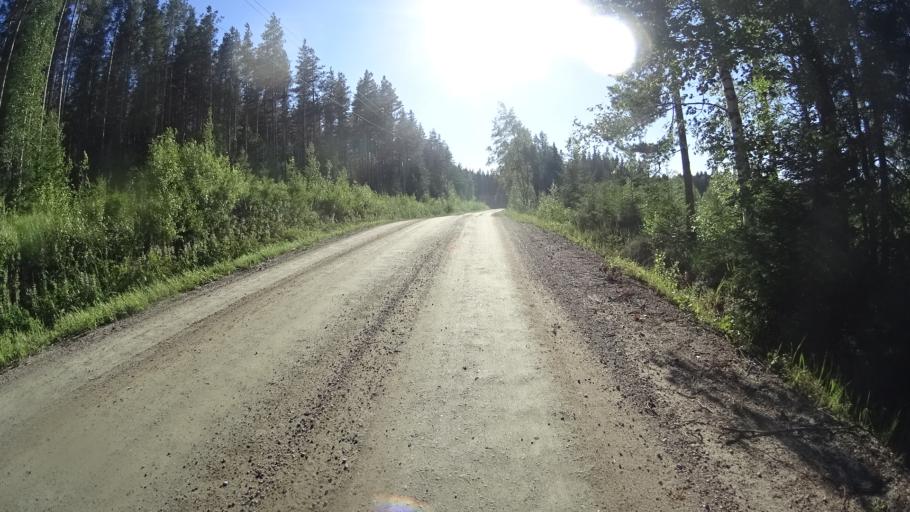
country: FI
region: Uusimaa
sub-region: Helsinki
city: Karkkila
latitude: 60.6477
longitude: 24.1584
